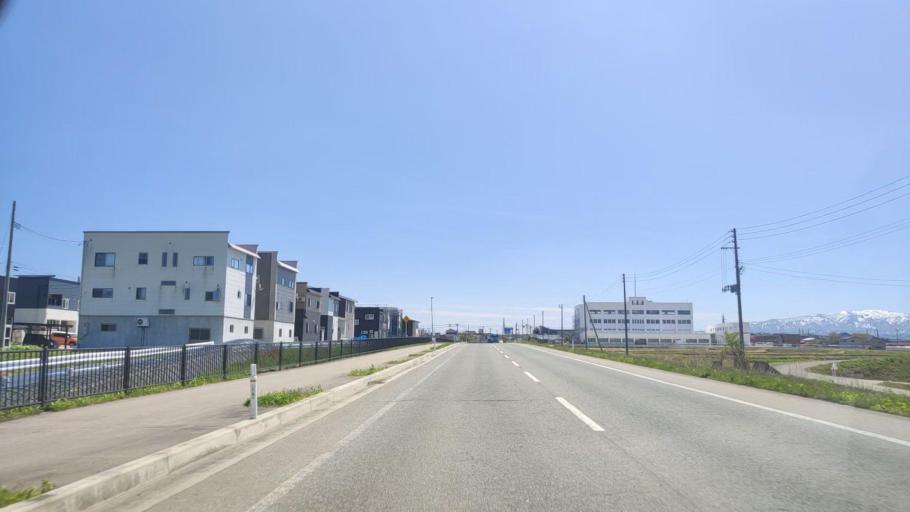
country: JP
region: Yamagata
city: Shinjo
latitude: 38.7542
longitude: 140.2943
